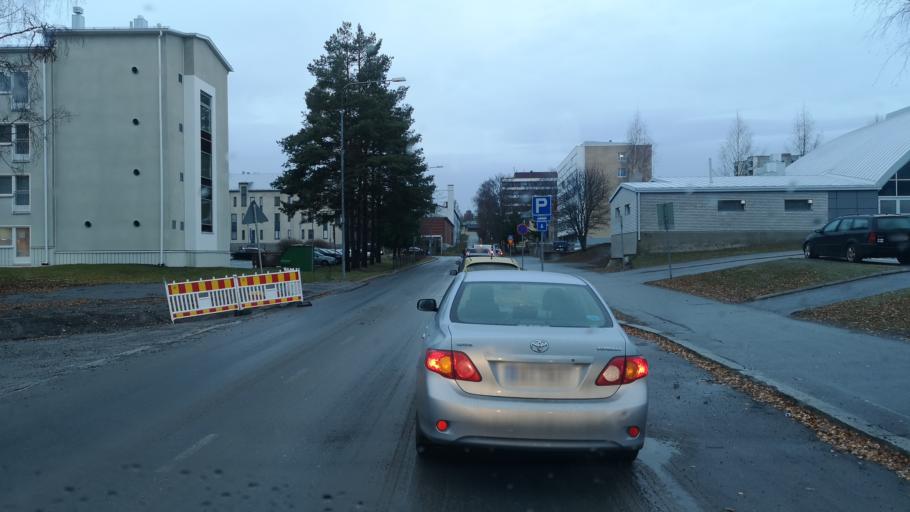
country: FI
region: Ostrobothnia
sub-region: Vaasa
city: Vaasa
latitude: 63.0860
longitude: 21.6196
